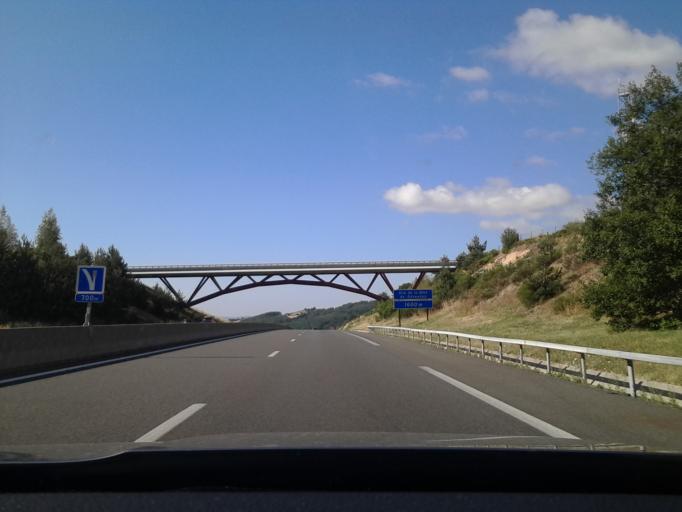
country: FR
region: Languedoc-Roussillon
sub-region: Departement de la Lozere
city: Marvejols
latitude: 44.5842
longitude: 3.2501
